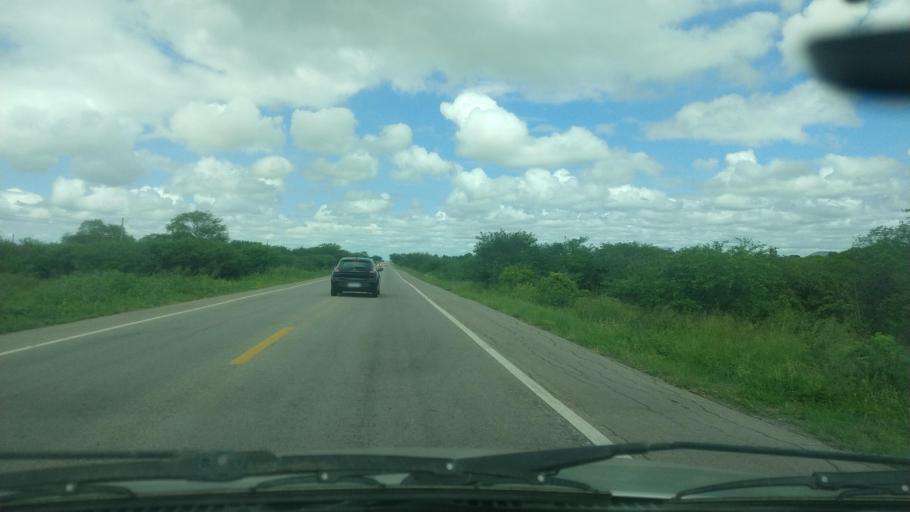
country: BR
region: Rio Grande do Norte
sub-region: Tangara
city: Tangara
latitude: -6.1654
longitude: -35.7572
